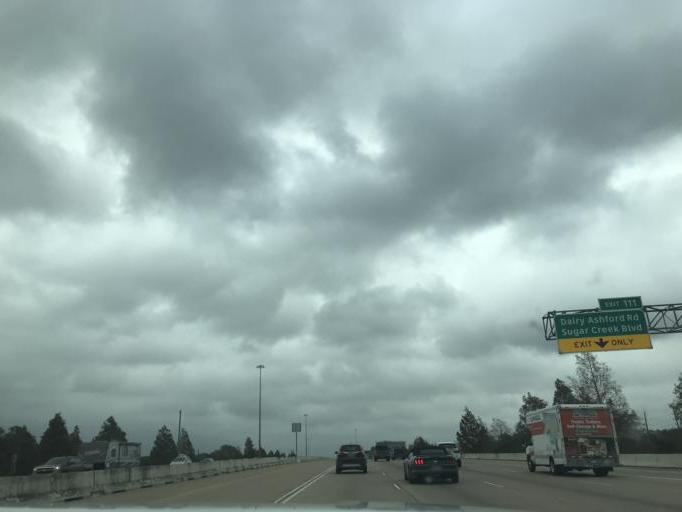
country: US
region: Texas
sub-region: Fort Bend County
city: Sugar Land
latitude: 29.6056
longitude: -95.6150
